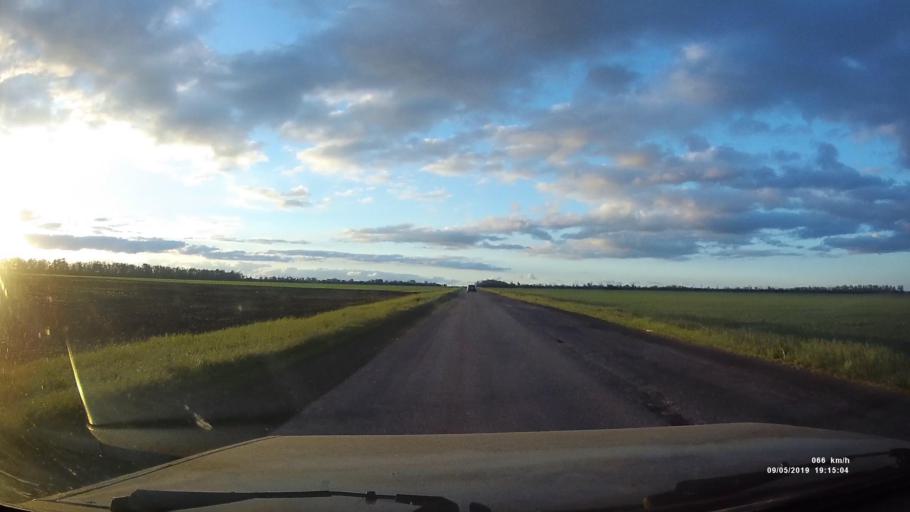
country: RU
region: Krasnodarskiy
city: Kanelovskaya
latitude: 46.7655
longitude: 39.2126
